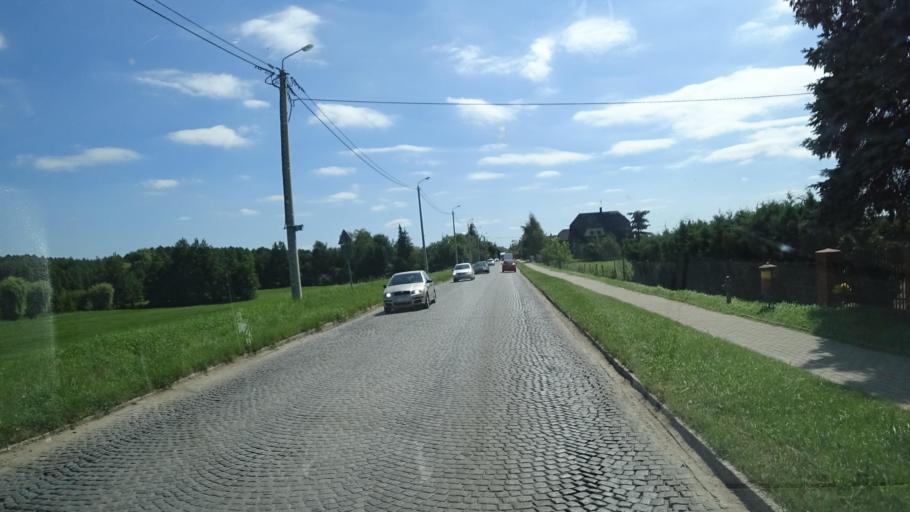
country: PL
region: Warmian-Masurian Voivodeship
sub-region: Powiat elcki
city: Prostki
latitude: 53.6932
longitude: 22.4422
